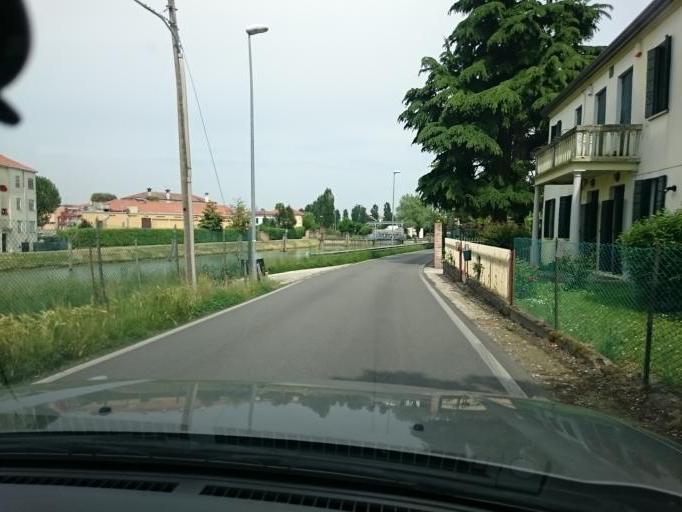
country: IT
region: Veneto
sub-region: Provincia di Venezia
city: Dolo
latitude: 45.4214
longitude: 12.0754
